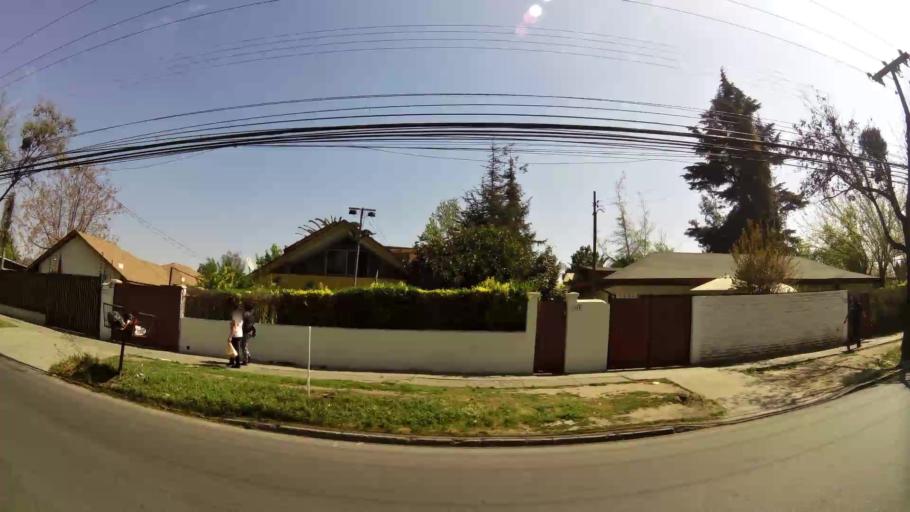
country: CL
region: Santiago Metropolitan
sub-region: Provincia de Santiago
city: Villa Presidente Frei, Nunoa, Santiago, Chile
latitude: -33.4405
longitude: -70.5619
